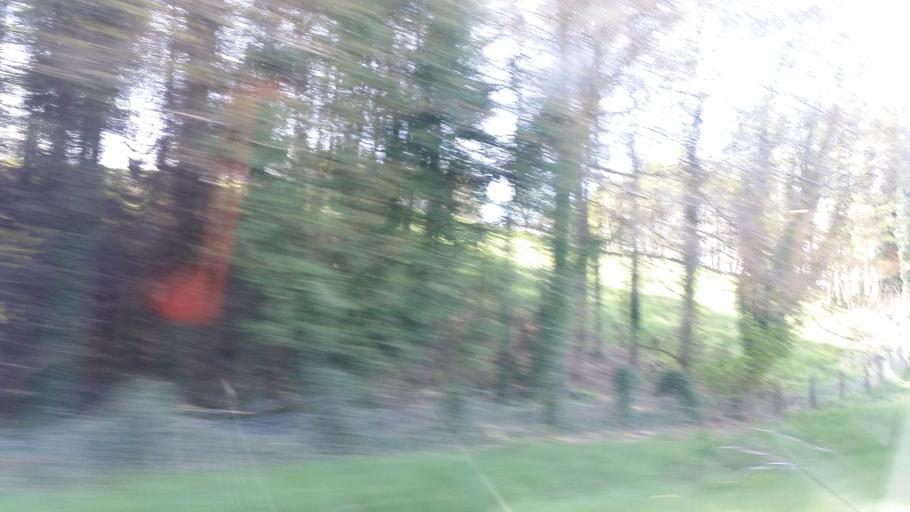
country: GB
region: Northern Ireland
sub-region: Fermanagh District
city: Enniskillen
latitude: 54.3709
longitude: -7.6843
